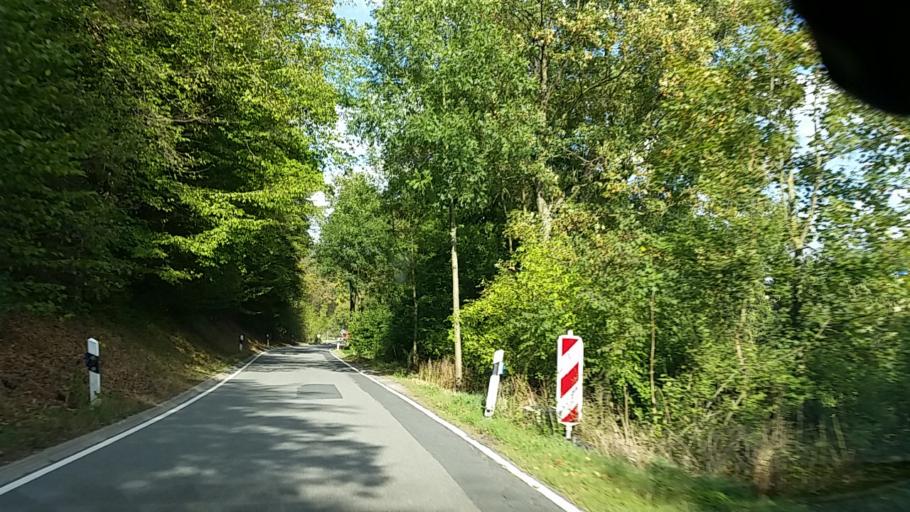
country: DE
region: Lower Saxony
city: Juhnde
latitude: 51.4419
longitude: 9.8506
